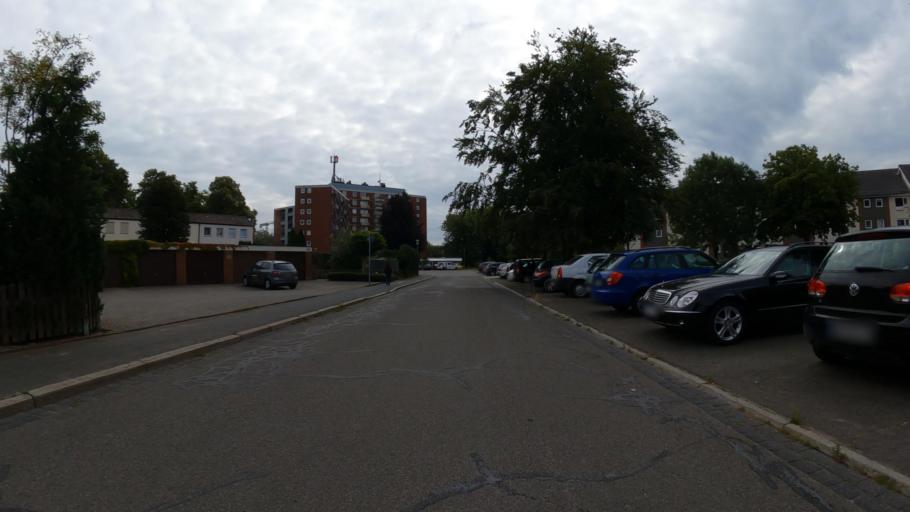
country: DE
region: Schleswig-Holstein
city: Neumunster
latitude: 54.0677
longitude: 9.9954
